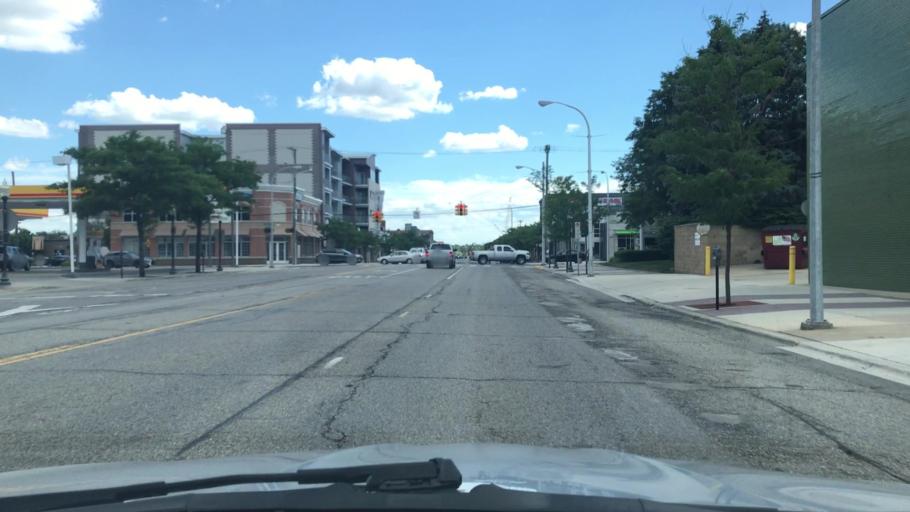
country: US
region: Michigan
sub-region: Oakland County
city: Royal Oak
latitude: 42.4843
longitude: -83.1442
